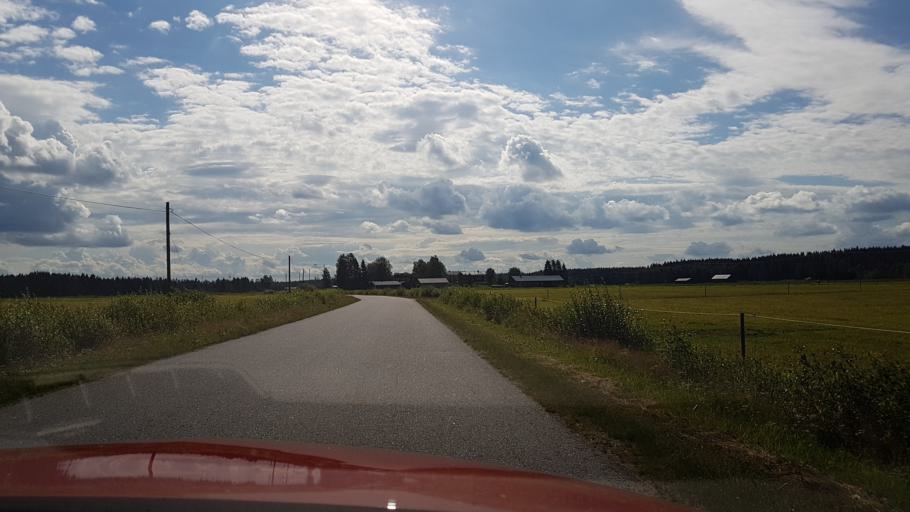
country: FI
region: Central Ostrobothnia
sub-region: Kokkola
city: Kannus
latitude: 64.0433
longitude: 23.8764
